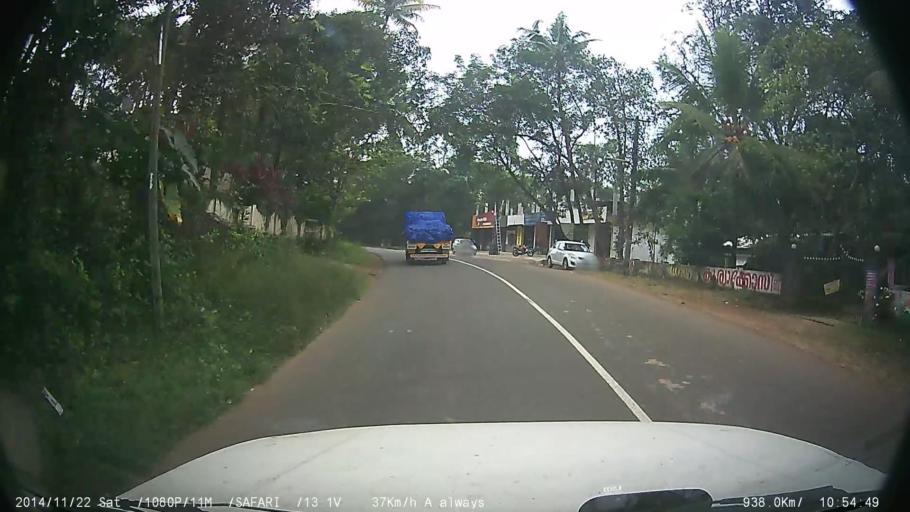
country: IN
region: Kerala
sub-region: Ernakulam
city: Muvattupuzha
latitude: 9.9554
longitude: 76.5750
